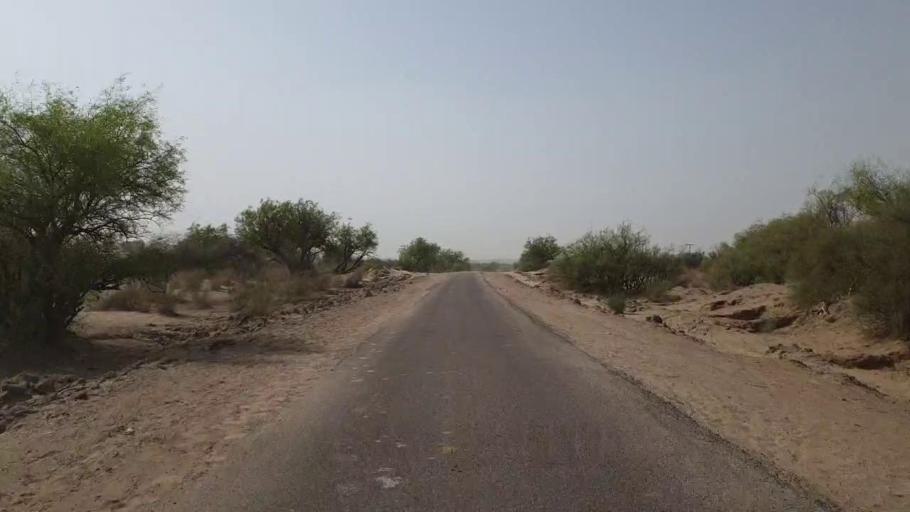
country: PK
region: Sindh
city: Mithi
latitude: 24.6045
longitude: 69.9221
